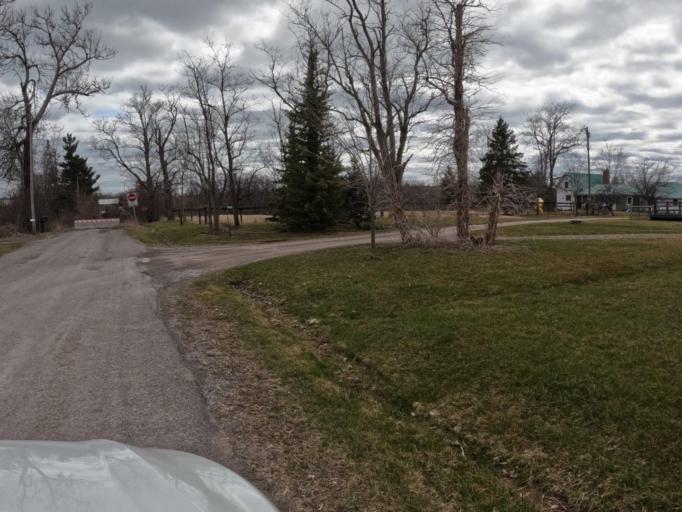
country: CA
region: Ontario
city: Norfolk County
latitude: 42.8266
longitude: -80.1696
